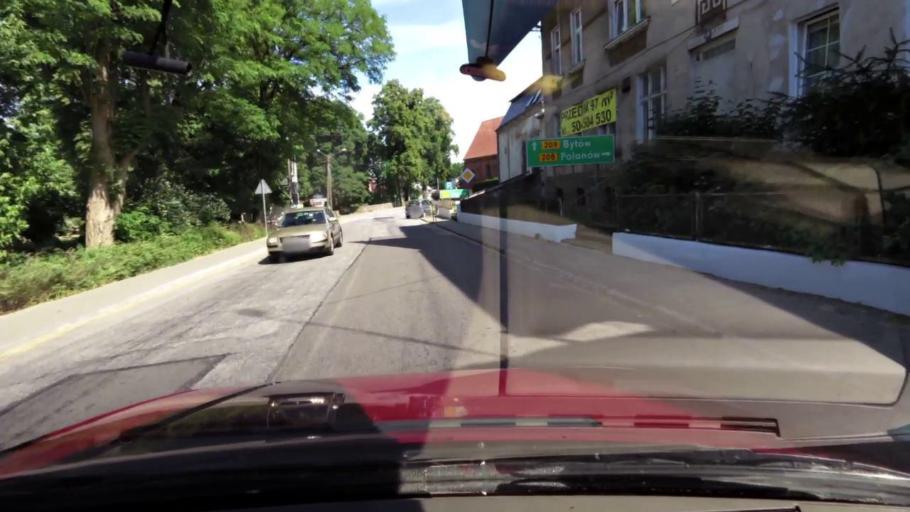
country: PL
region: Pomeranian Voivodeship
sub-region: Powiat slupski
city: Kepice
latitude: 54.2774
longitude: 16.9616
